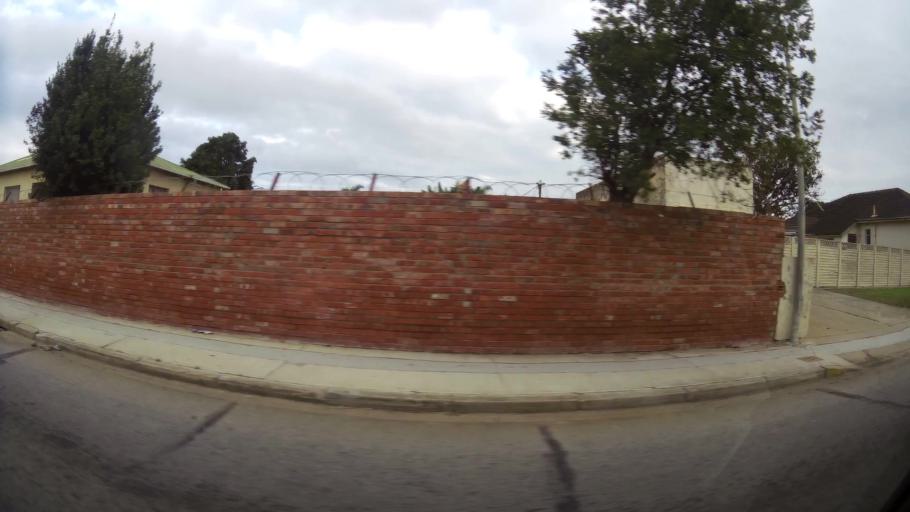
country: ZA
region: Eastern Cape
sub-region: Nelson Mandela Bay Metropolitan Municipality
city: Port Elizabeth
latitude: -33.9421
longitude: 25.5519
